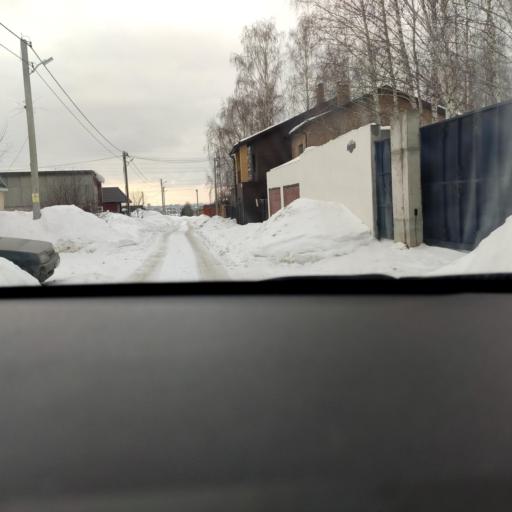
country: RU
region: Tatarstan
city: Vysokaya Gora
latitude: 55.8076
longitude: 49.2809
